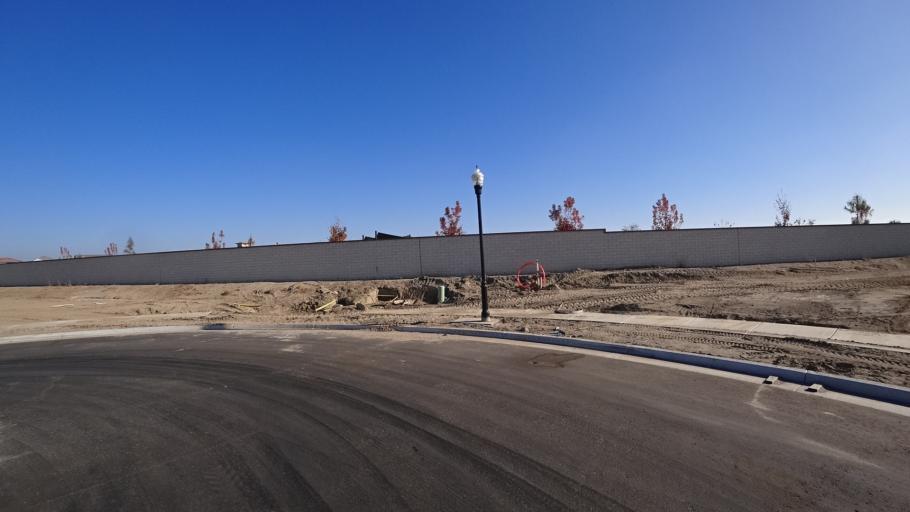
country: US
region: California
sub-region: Kern County
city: Rosedale
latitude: 35.3199
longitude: -119.1372
